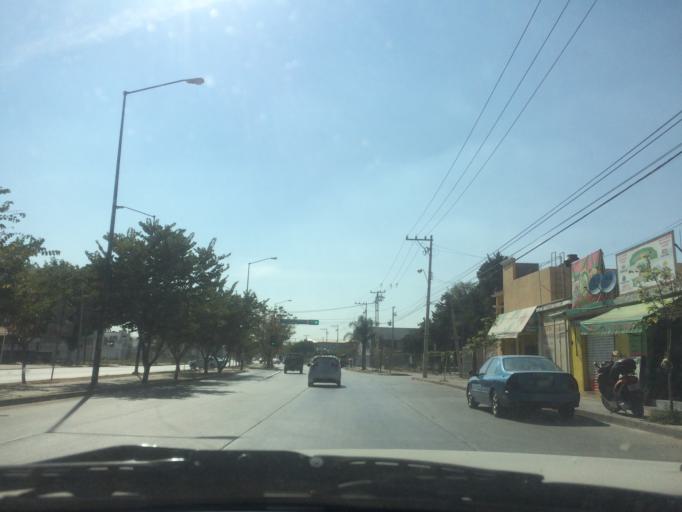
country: MX
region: Guanajuato
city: Leon
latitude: 21.1671
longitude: -101.6616
